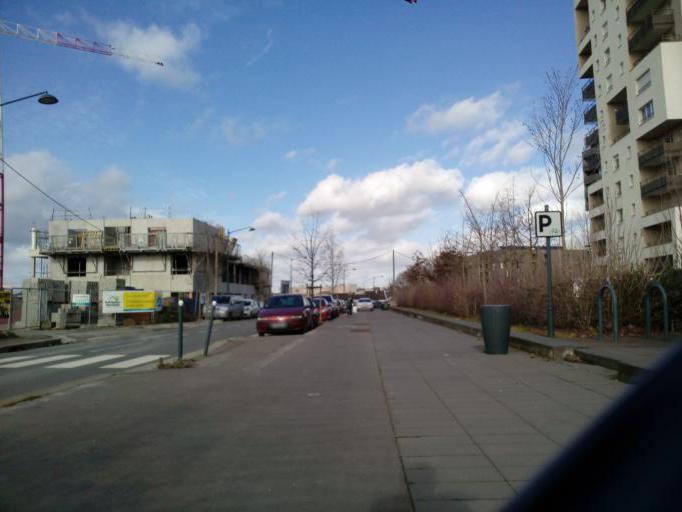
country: FR
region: Brittany
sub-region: Departement d'Ille-et-Vilaine
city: Rennes
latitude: 48.0997
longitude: -1.6986
